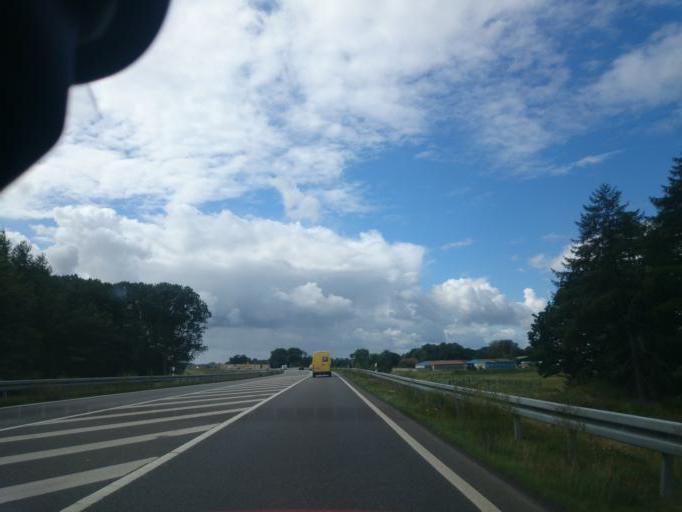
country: DE
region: Mecklenburg-Vorpommern
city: Samtens
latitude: 54.3573
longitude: 13.3085
